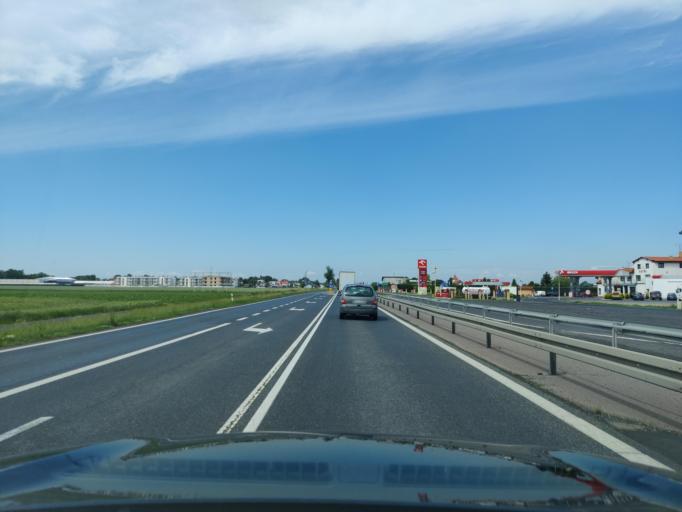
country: PL
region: Greater Poland Voivodeship
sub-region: Powiat grodziski
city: Granowo
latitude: 52.2220
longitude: 16.5457
